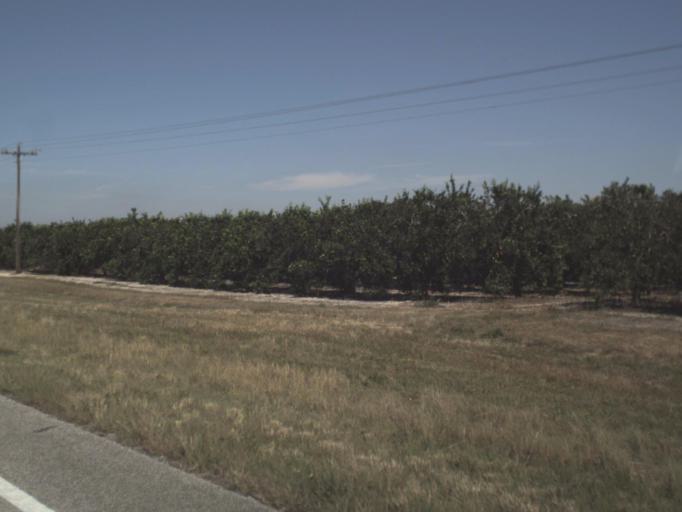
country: US
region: Florida
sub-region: Highlands County
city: Placid Lakes
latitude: 27.2044
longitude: -81.3286
